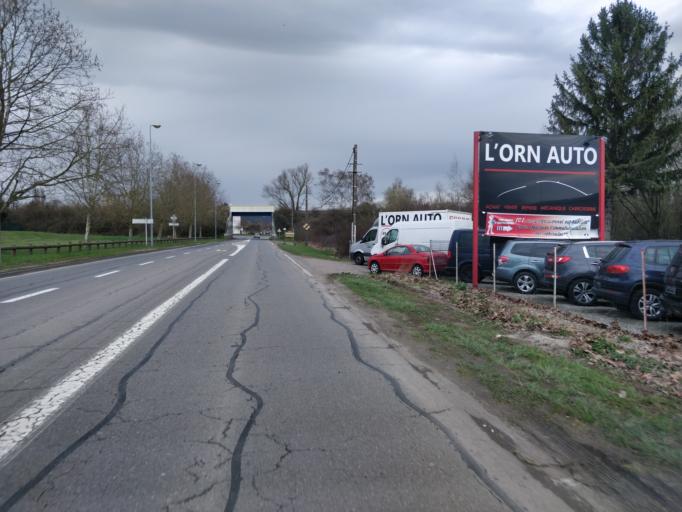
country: FR
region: Lorraine
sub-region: Departement de la Moselle
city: Uckange
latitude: 49.3253
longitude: 6.1535
